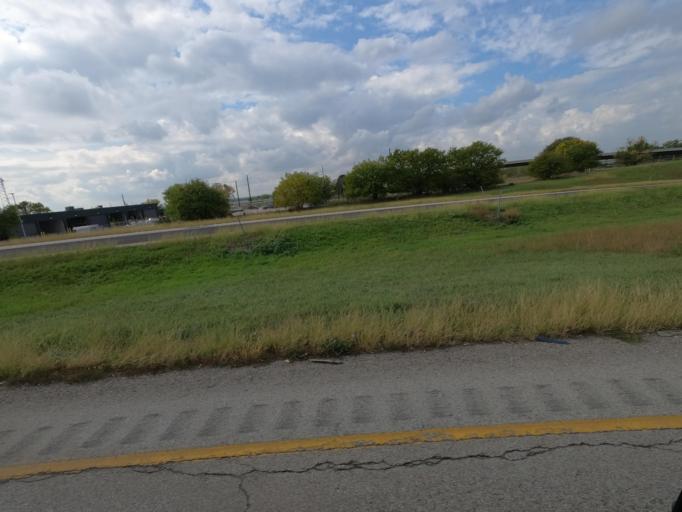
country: US
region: Iowa
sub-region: Polk County
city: Des Moines
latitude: 41.6498
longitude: -93.5791
